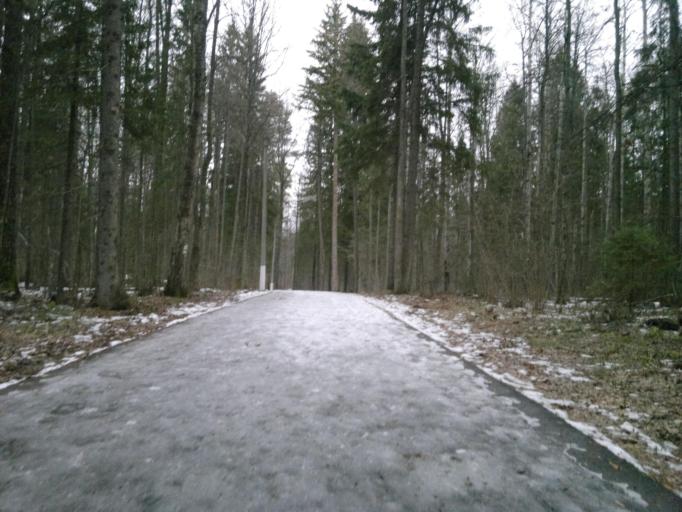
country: RU
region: Mariy-El
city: Yoshkar-Ola
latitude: 56.6013
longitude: 47.9651
